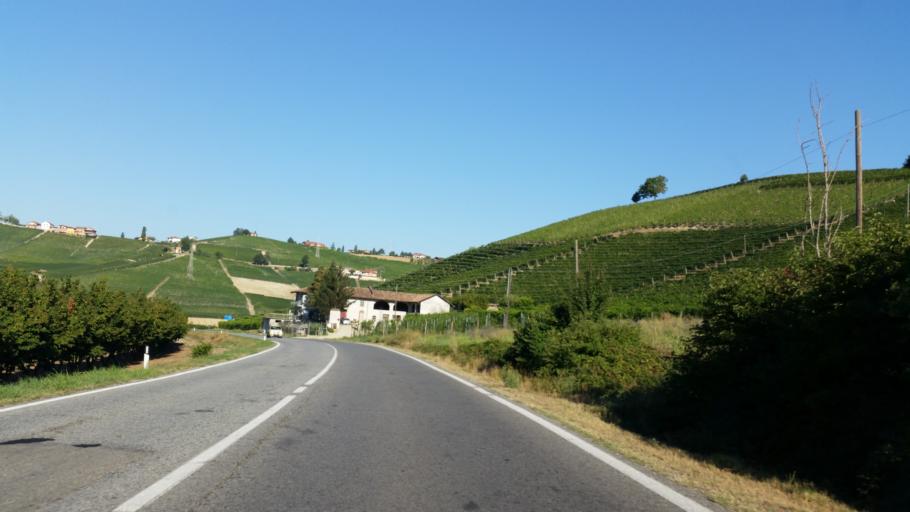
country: IT
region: Piedmont
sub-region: Provincia di Cuneo
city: Neive-Borgonovo
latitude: 44.7277
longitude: 8.1002
